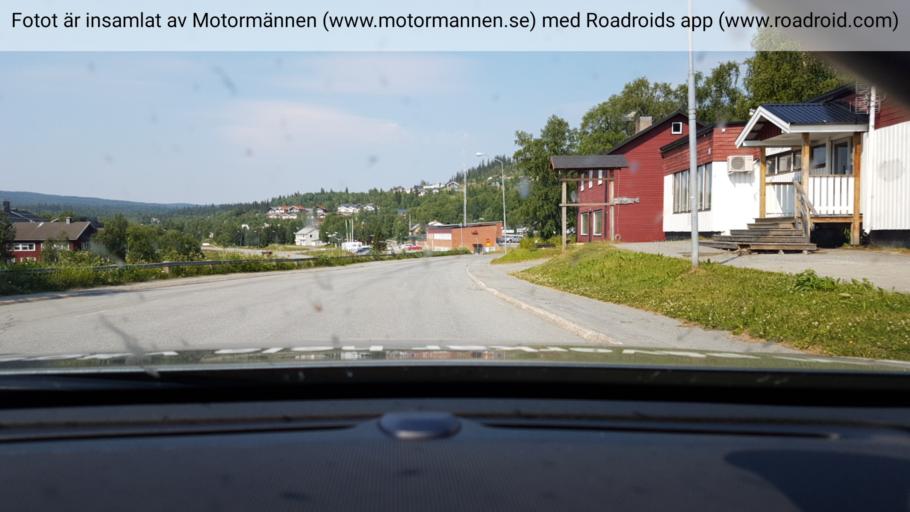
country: NO
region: Nordland
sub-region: Rana
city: Mo i Rana
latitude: 65.7143
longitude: 15.2602
